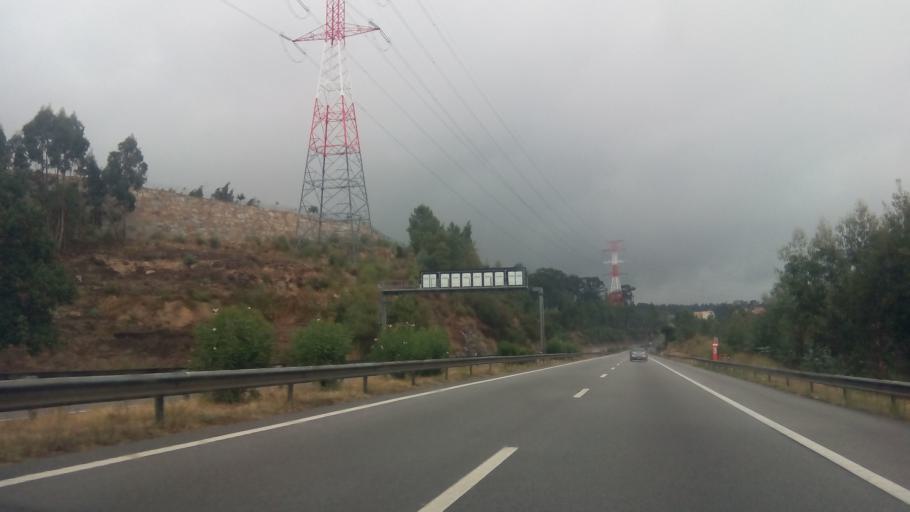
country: PT
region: Porto
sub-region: Paredes
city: Baltar
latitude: 41.1777
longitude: -8.3776
